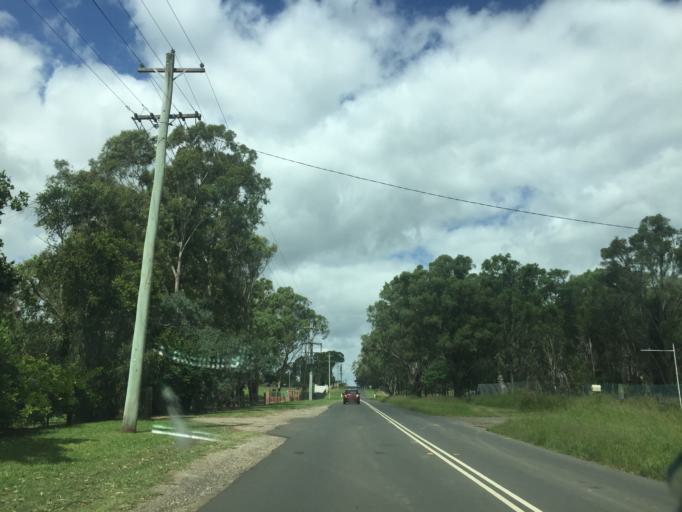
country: AU
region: New South Wales
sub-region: Penrith Municipality
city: Kingswood Park
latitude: -33.7960
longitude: 150.7151
